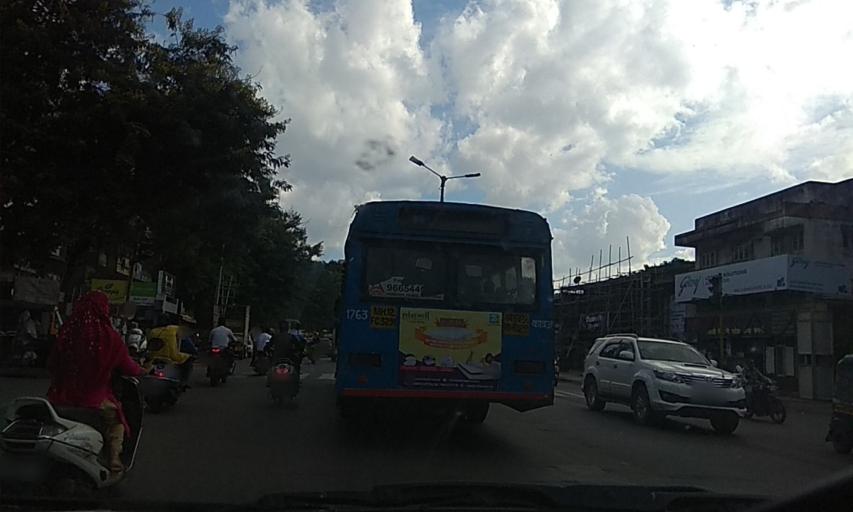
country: IN
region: Maharashtra
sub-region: Pune Division
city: Pune
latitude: 18.5073
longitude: 73.8684
